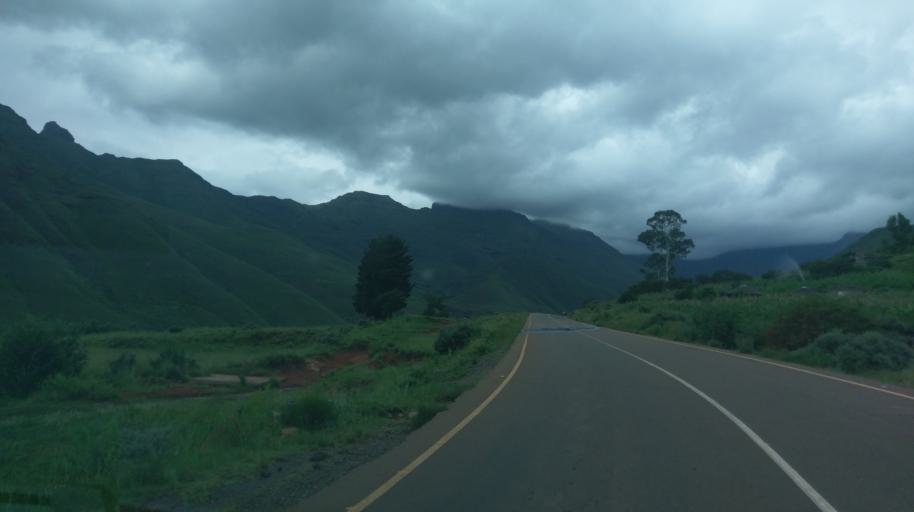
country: LS
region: Butha-Buthe
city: Butha-Buthe
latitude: -29.0506
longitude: 28.3320
